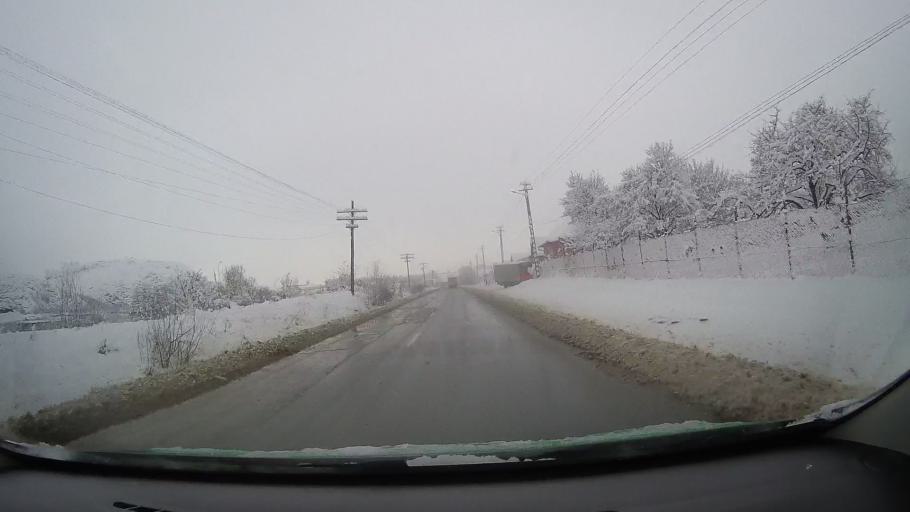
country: RO
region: Sibiu
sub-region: Comuna Orlat
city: Orlat
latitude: 45.7562
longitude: 23.9545
